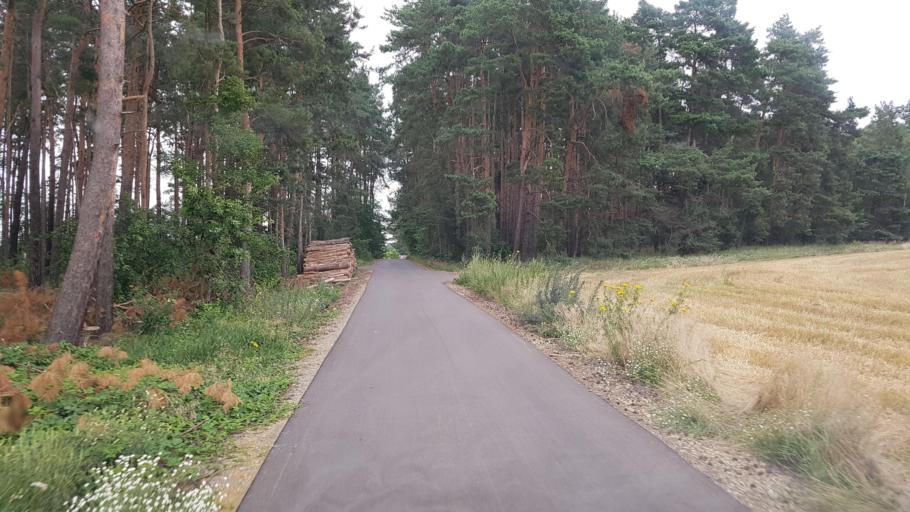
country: DE
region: Brandenburg
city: Grossraschen
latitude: 51.6079
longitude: 14.0430
